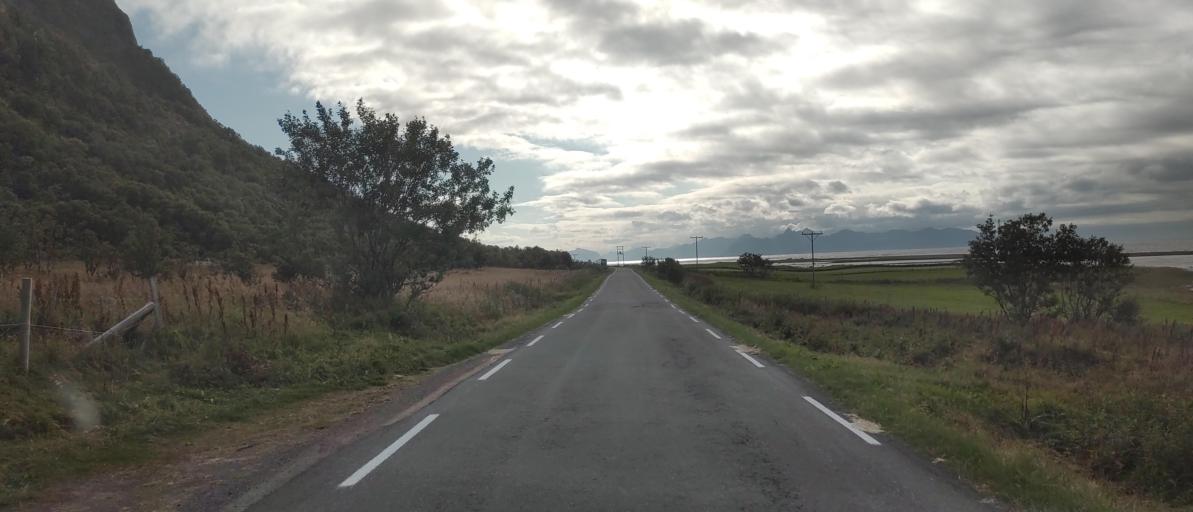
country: NO
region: Nordland
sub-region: Sortland
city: Sortland
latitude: 69.0716
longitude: 15.5500
